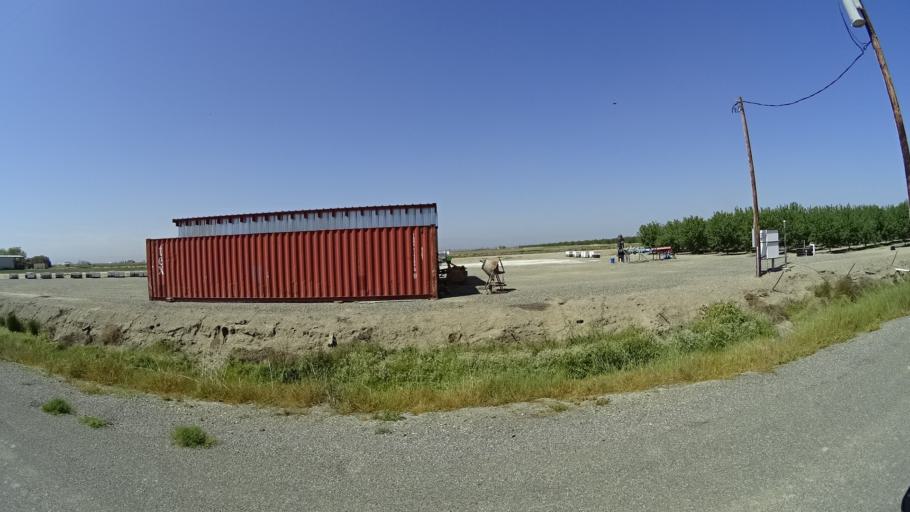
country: US
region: California
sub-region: Glenn County
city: Willows
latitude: 39.5093
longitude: -122.1028
